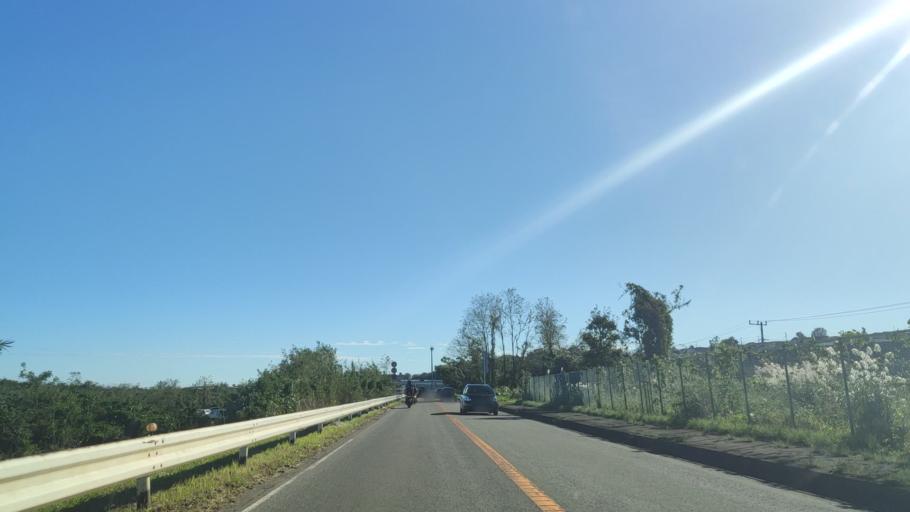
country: JP
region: Kanagawa
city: Zama
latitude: 35.5000
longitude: 139.3714
